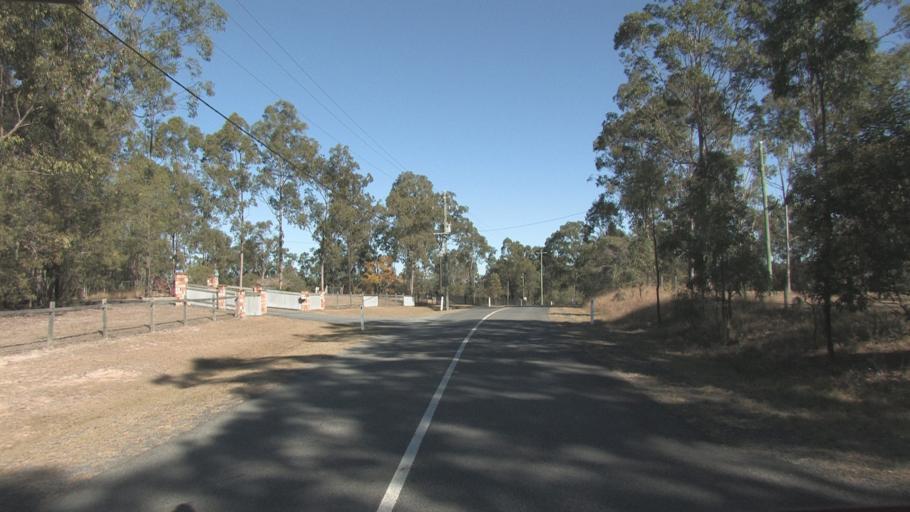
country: AU
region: Queensland
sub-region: Logan
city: North Maclean
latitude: -27.8118
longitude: 152.9709
